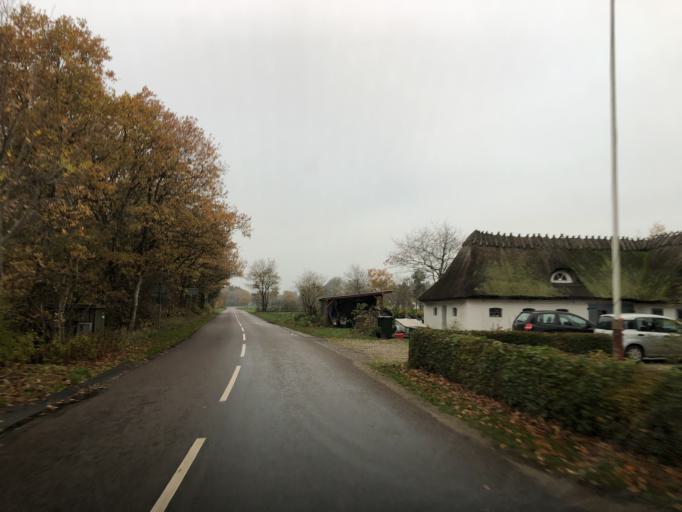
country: DK
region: Central Jutland
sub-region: Herning Kommune
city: Avlum
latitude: 56.2477
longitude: 8.8777
